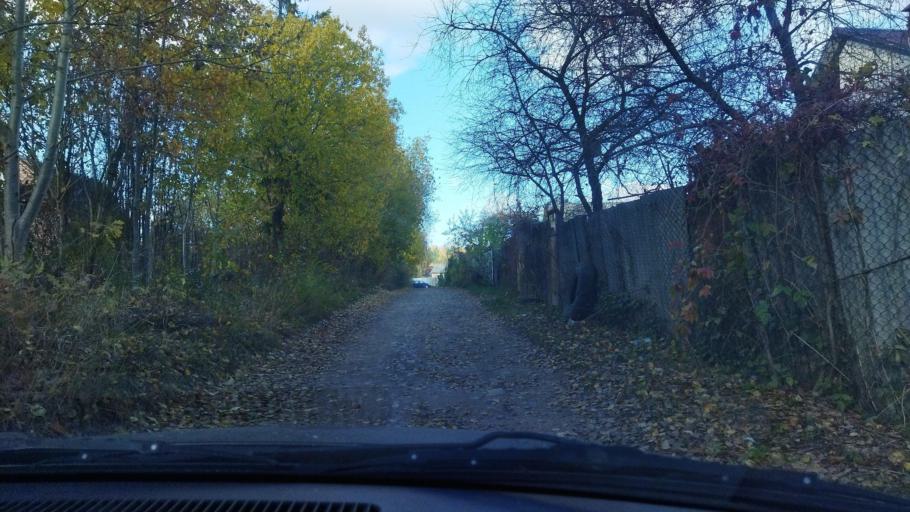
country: BY
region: Minsk
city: Slabada
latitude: 53.9872
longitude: 27.8996
